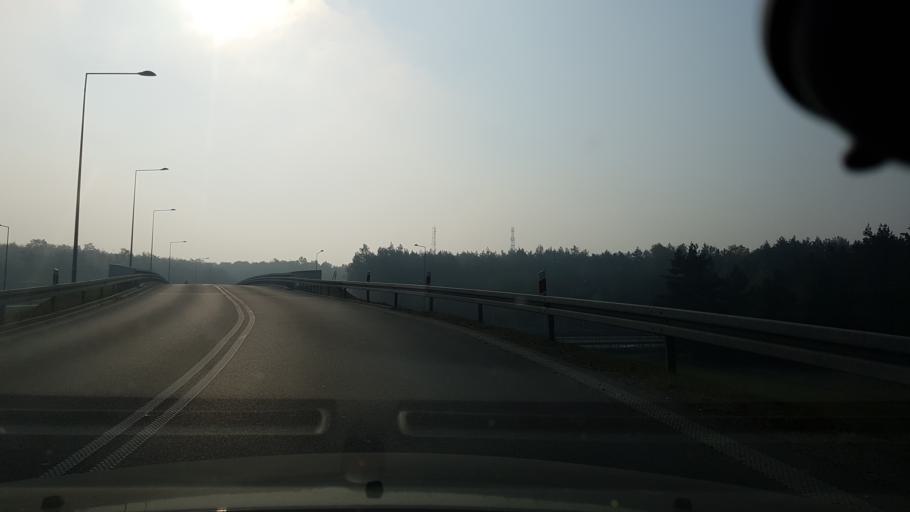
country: PL
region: Lodz Voivodeship
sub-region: Powiat tomaszowski
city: Tomaszow Mazowiecki
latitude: 51.5662
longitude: 20.0203
